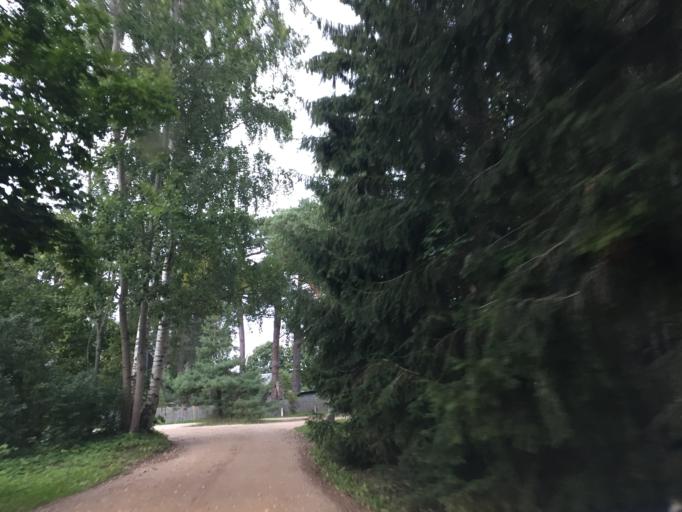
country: LV
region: Saulkrastu
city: Saulkrasti
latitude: 57.3330
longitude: 24.4063
